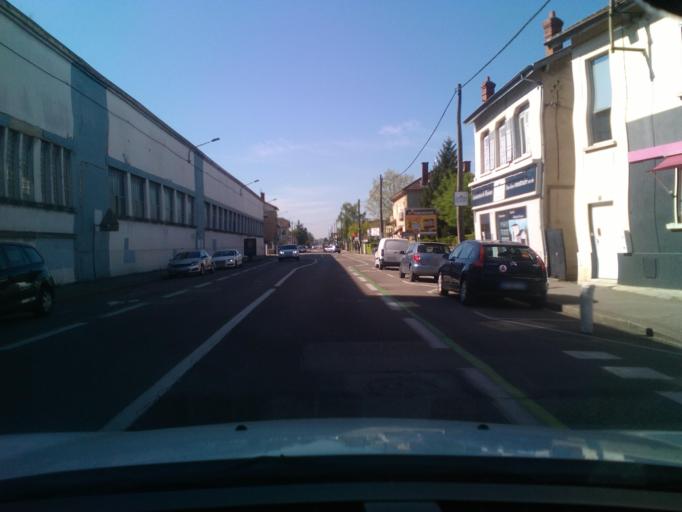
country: FR
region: Rhone-Alpes
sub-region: Departement de l'Ain
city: Peronnas
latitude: 46.1928
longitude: 5.2131
